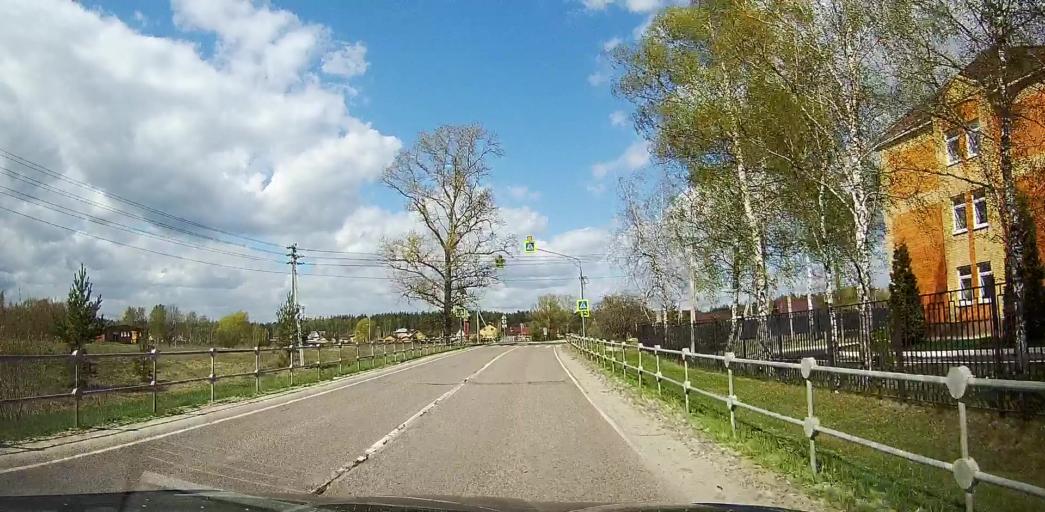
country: RU
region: Moskovskaya
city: Davydovo
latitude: 55.5583
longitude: 38.8135
